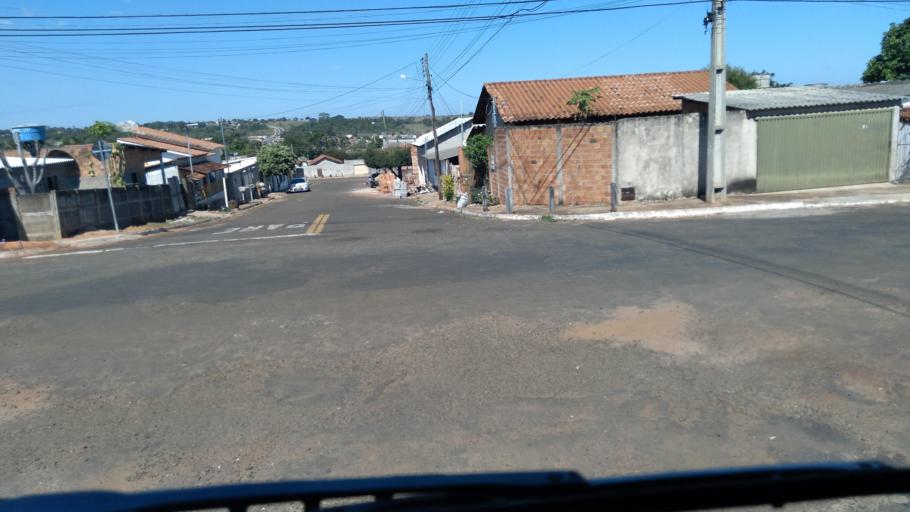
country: BR
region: Goias
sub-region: Mineiros
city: Mineiros
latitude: -17.5728
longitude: -52.5678
